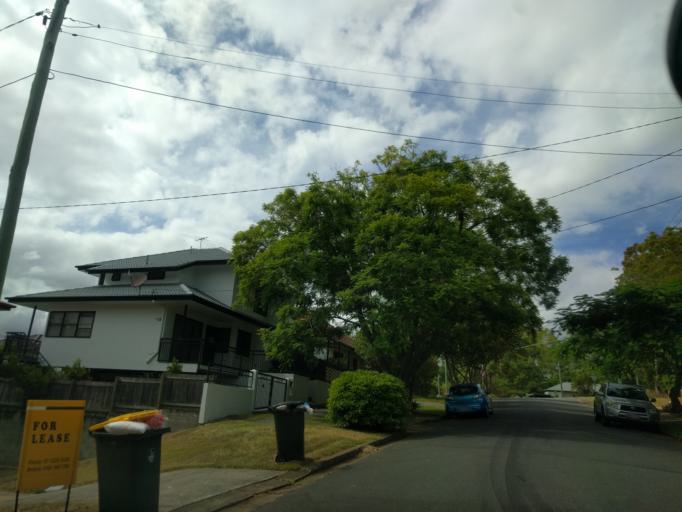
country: AU
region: Queensland
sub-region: Brisbane
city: Toowong
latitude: -27.4973
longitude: 153.0044
